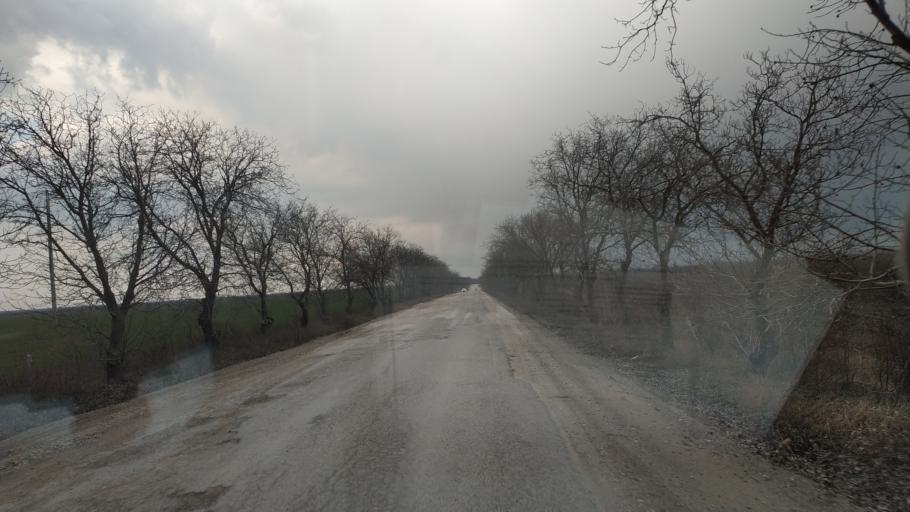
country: MD
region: Telenesti
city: Grigoriopol
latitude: 47.0340
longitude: 29.2927
